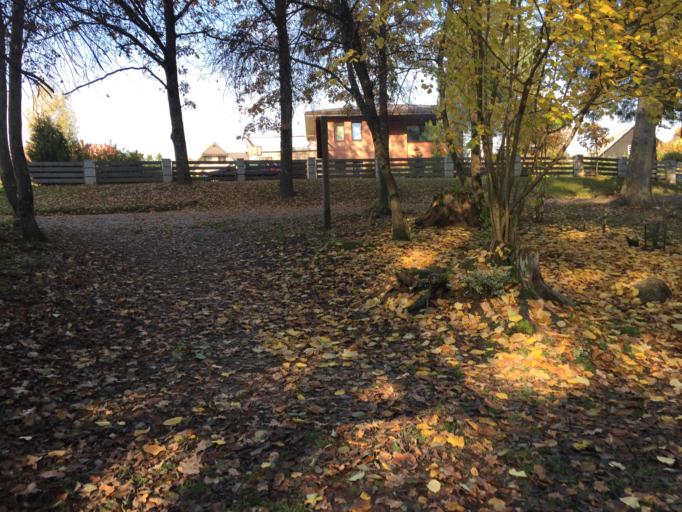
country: LV
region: Saldus Rajons
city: Saldus
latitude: 56.6488
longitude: 22.4877
